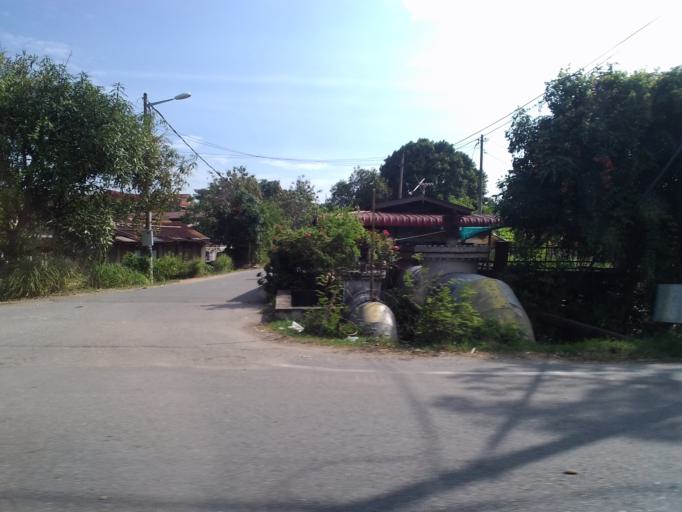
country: MY
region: Kedah
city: Gurun
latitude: 5.9532
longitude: 100.4078
